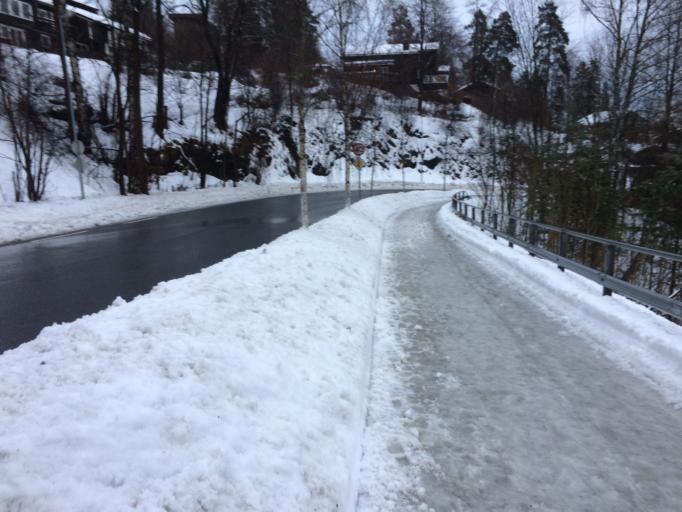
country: NO
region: Akershus
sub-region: Asker
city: Billingstad
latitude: 59.8748
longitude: 10.4850
